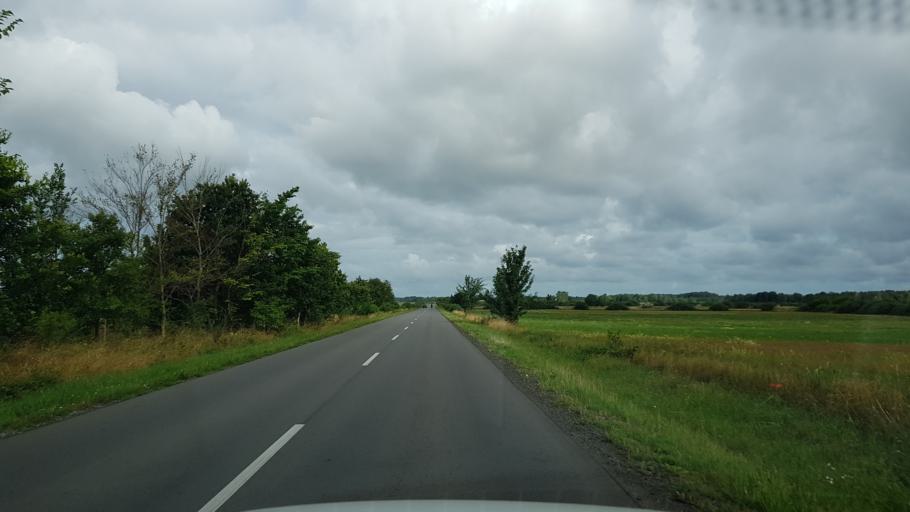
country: PL
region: West Pomeranian Voivodeship
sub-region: Powiat gryficki
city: Karnice
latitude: 54.0401
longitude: 15.0390
